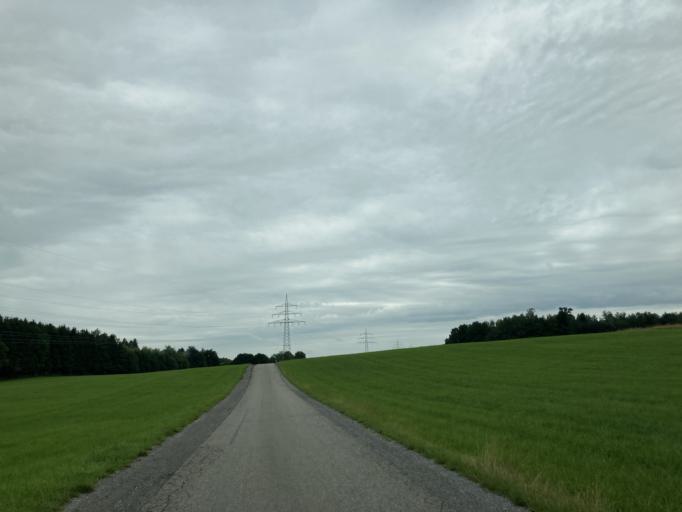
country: DE
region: Bavaria
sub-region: Upper Bavaria
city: Stephanskirchen
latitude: 47.8628
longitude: 12.1938
